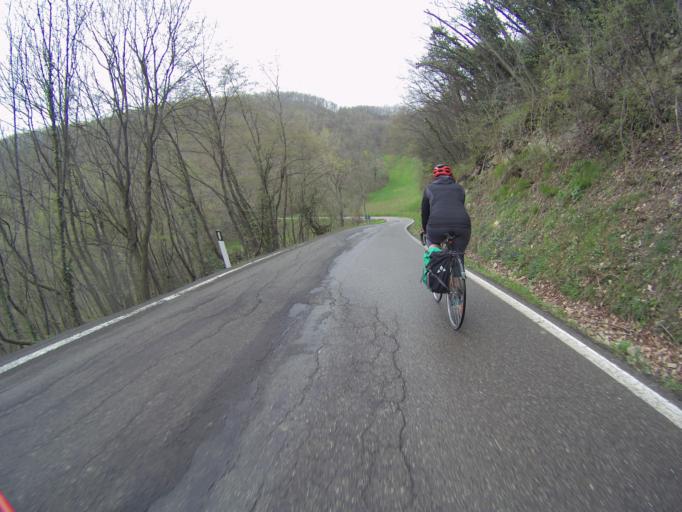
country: IT
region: Emilia-Romagna
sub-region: Provincia di Reggio Emilia
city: Ciano d'Enza
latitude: 44.5624
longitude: 10.4504
